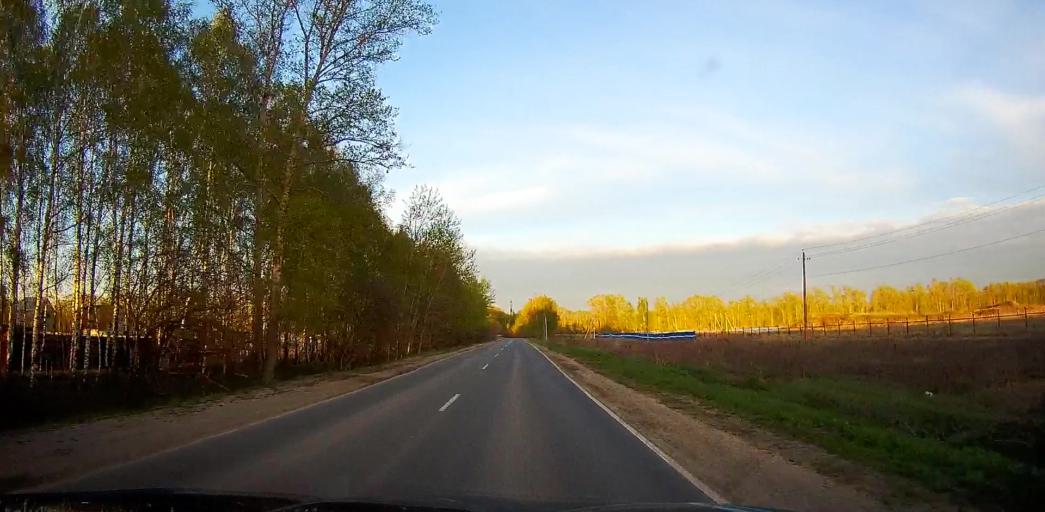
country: RU
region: Moskovskaya
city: Peski
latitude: 55.2097
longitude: 38.7056
